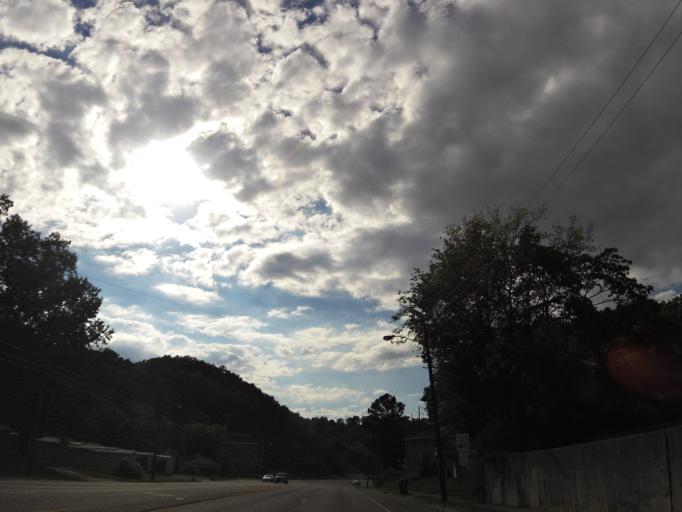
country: US
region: Georgia
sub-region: Catoosa County
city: Lakeview
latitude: 34.9765
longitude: -85.2727
